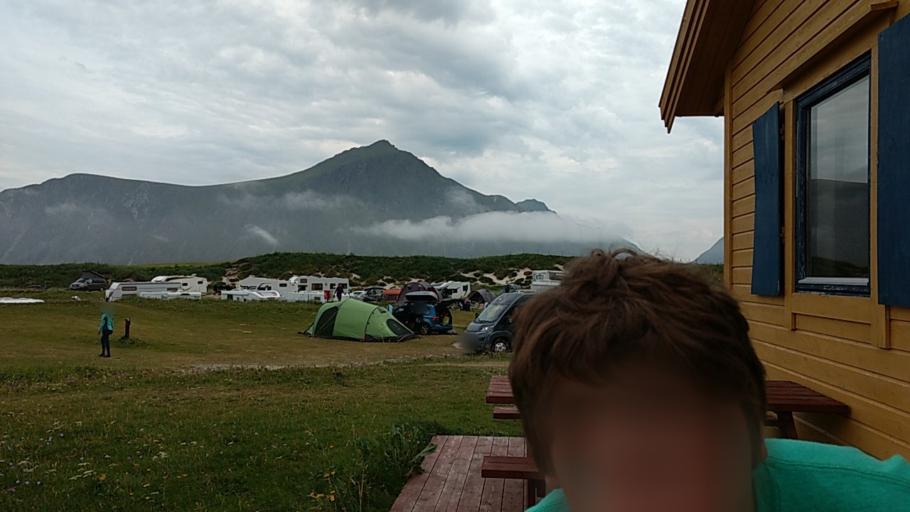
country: NO
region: Nordland
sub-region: Flakstad
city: Ramberg
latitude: 68.1033
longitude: 13.2936
